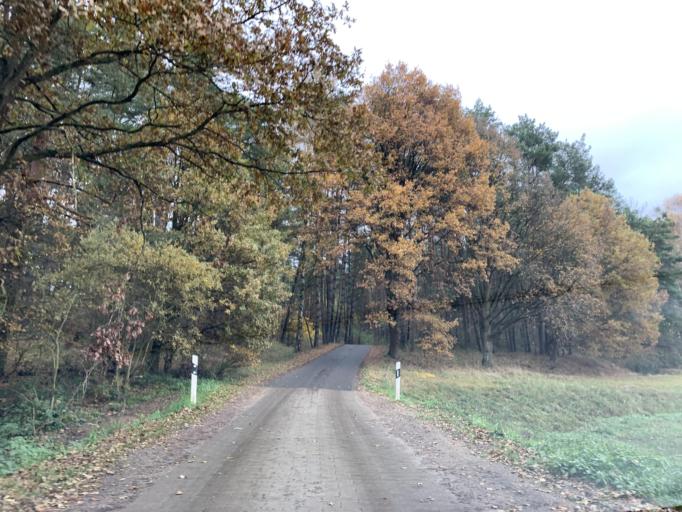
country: DE
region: Mecklenburg-Vorpommern
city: Blankensee
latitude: 53.3921
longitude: 13.2682
